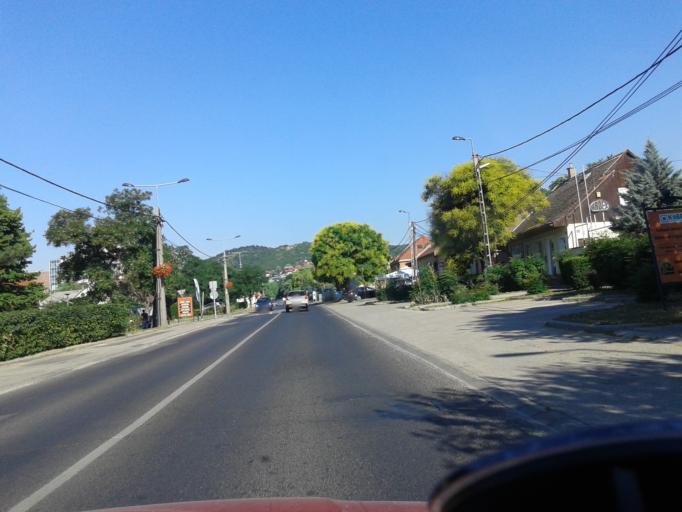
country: HU
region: Pest
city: Budaors
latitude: 47.4604
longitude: 18.9518
